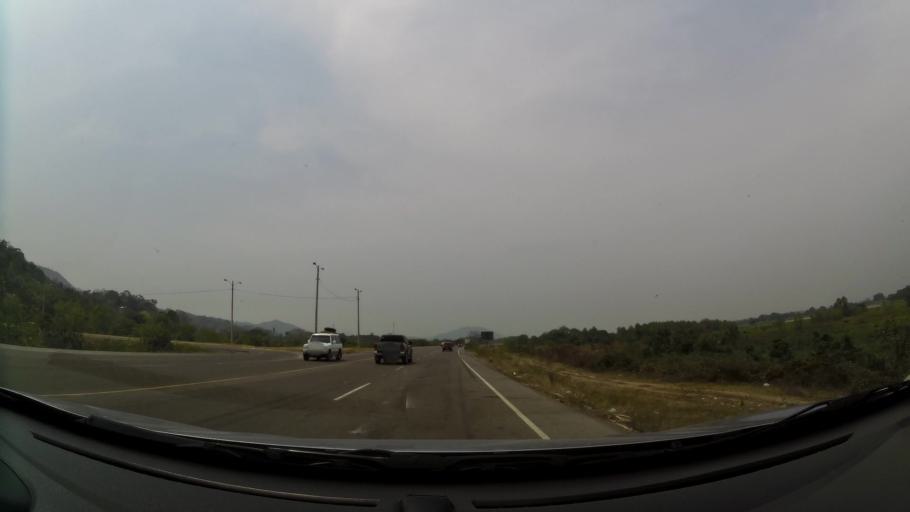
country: HN
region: Cortes
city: Potrerillos
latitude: 15.2198
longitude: -87.9624
